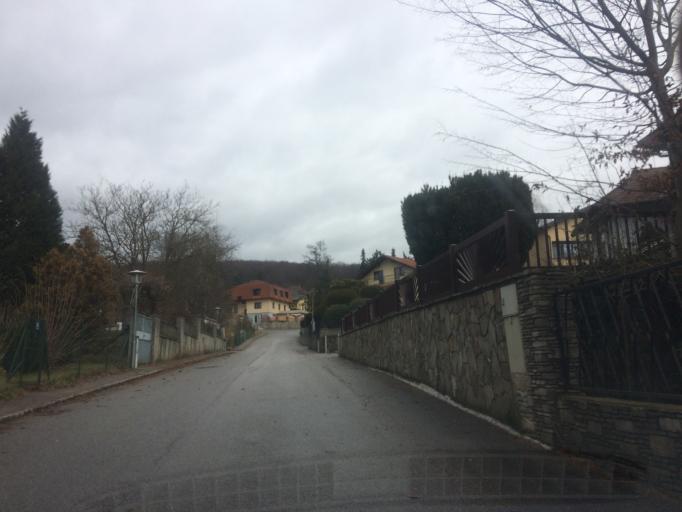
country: AT
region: Lower Austria
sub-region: Politischer Bezirk Wien-Umgebung
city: Gablitz
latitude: 48.2319
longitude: 16.1508
